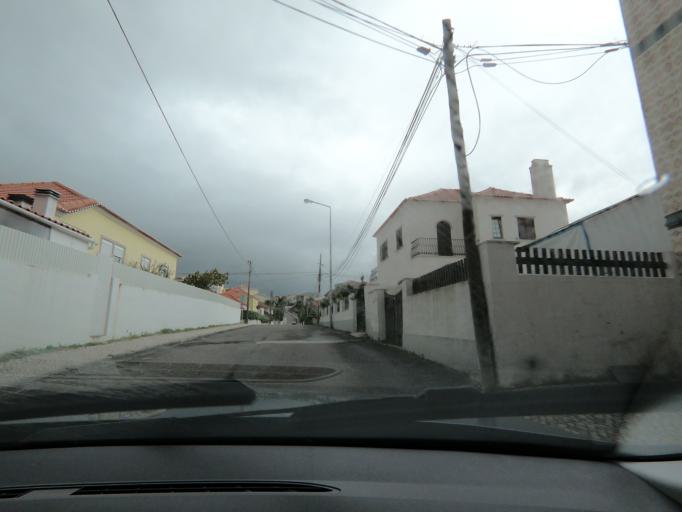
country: PT
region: Lisbon
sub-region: Sintra
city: Rio de Mouro
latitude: 38.7986
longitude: -9.3394
